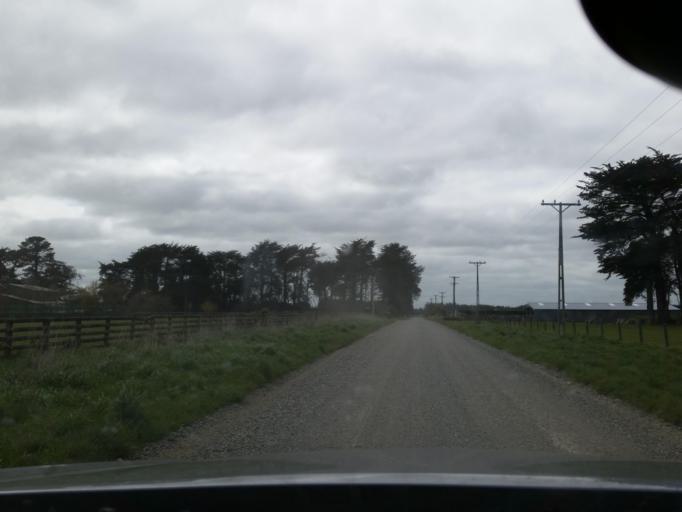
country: NZ
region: Southland
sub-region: Invercargill City
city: Invercargill
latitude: -46.3557
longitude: 168.4373
